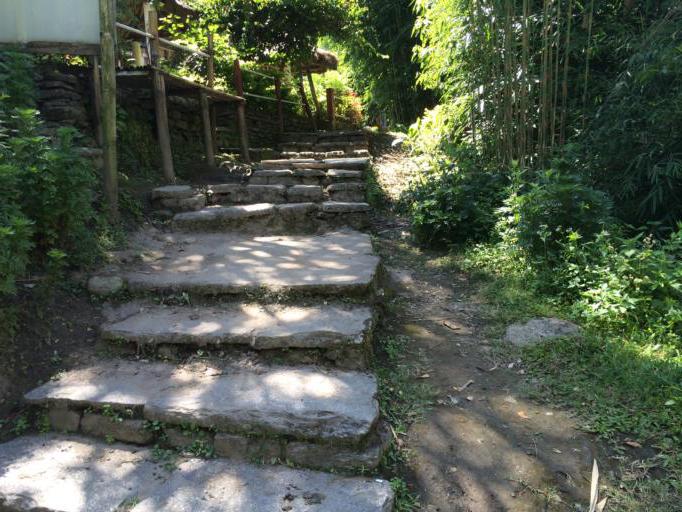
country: NP
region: Western Region
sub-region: Gandaki Zone
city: Khudi
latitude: 28.3847
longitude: 84.4030
